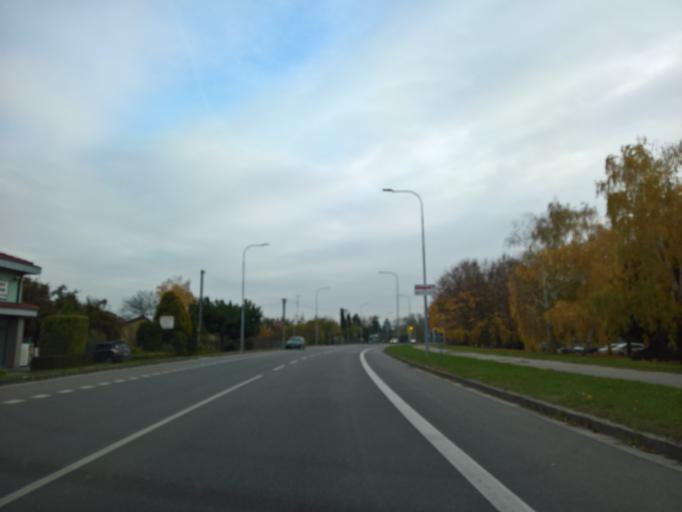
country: SK
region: Nitriansky
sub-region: Okres Nitra
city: Nitra
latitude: 48.3082
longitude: 18.1156
